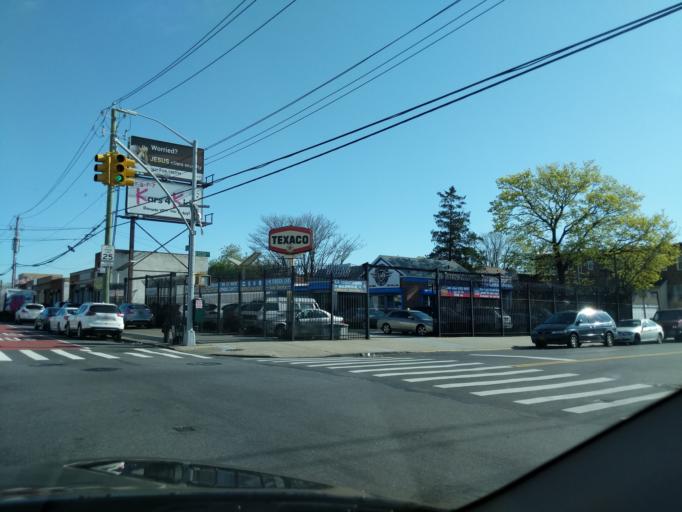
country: US
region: New York
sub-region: Kings County
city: Brooklyn
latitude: 40.6397
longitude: -73.9291
